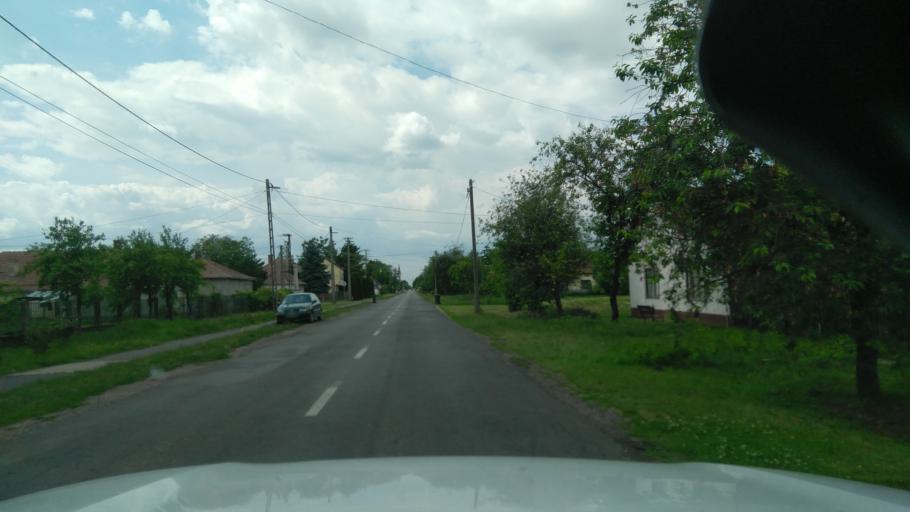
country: HU
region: Bekes
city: Magyarbanhegyes
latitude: 46.4501
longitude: 20.9755
